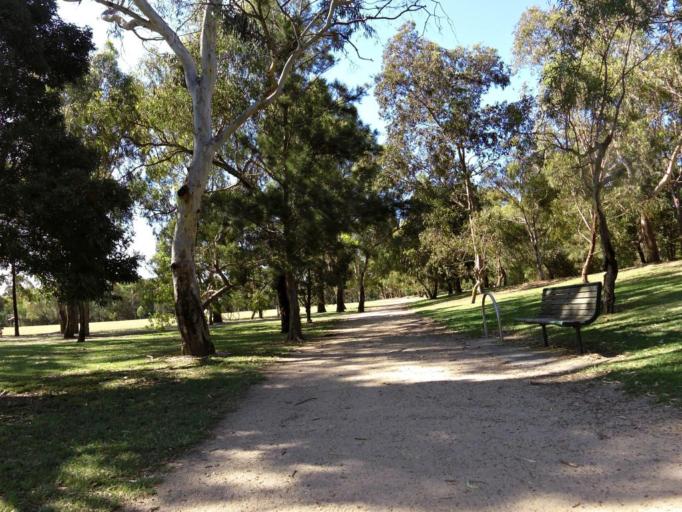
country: AU
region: Victoria
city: Ivanhoe East
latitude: -37.7890
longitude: 145.0597
